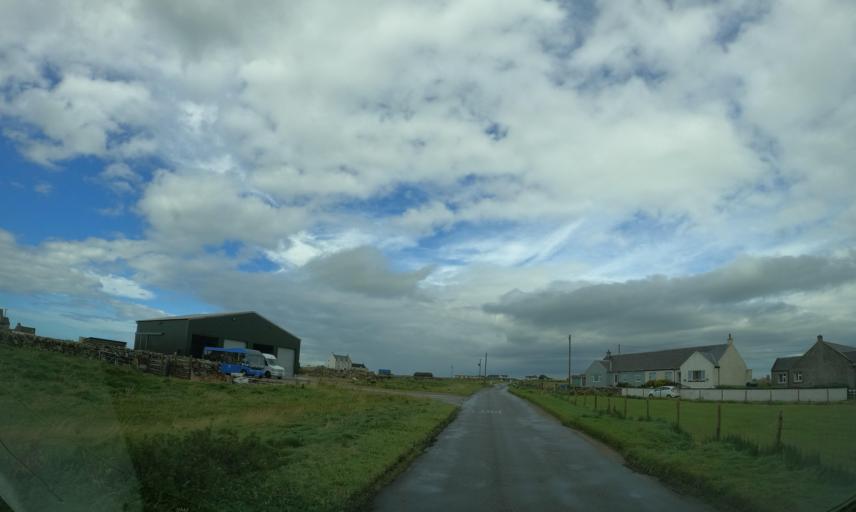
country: GB
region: Scotland
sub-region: Eilean Siar
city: Barra
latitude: 56.4899
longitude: -6.8809
